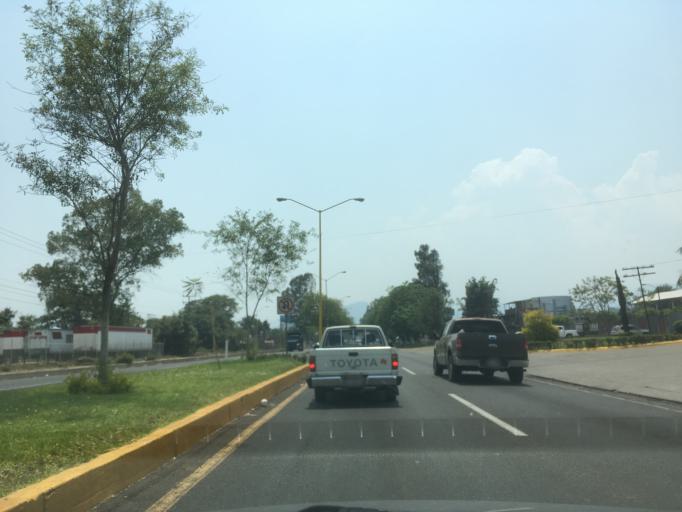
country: MX
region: Michoacan
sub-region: Uruapan
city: Uruapan
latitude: 19.4225
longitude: -102.0331
